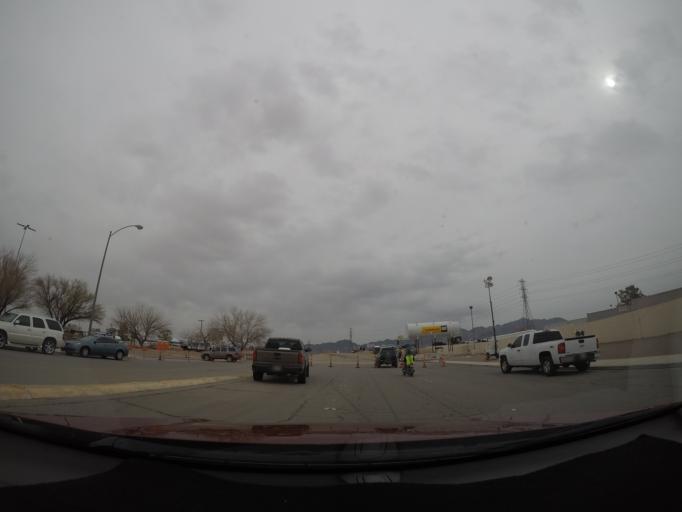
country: US
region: Nevada
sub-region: Clark County
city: Sandy Valley
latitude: 35.6135
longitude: -115.3809
